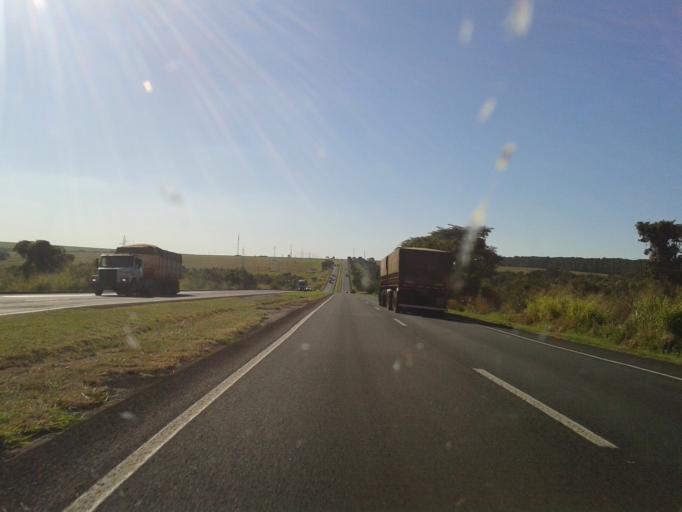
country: BR
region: Minas Gerais
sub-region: Uberlandia
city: Uberlandia
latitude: -19.0941
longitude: -48.1832
